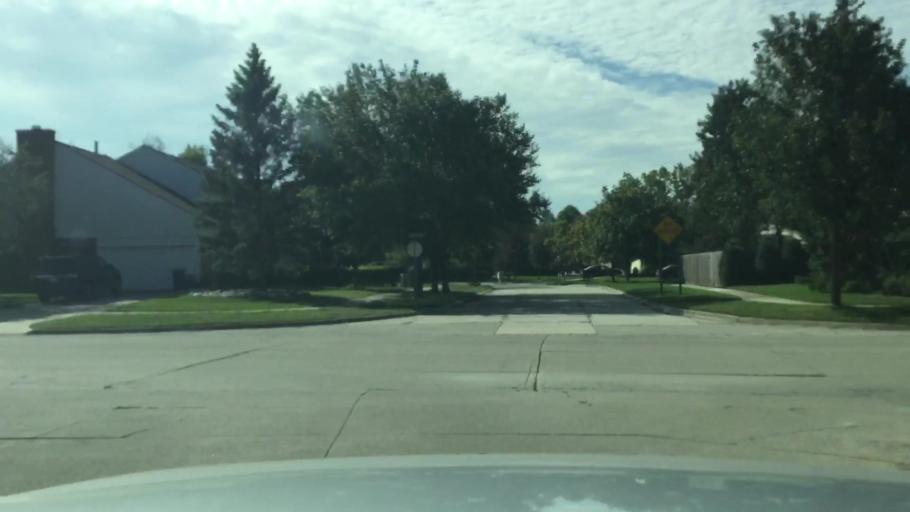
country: US
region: Michigan
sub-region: Wayne County
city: Canton
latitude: 42.3297
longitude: -83.4913
